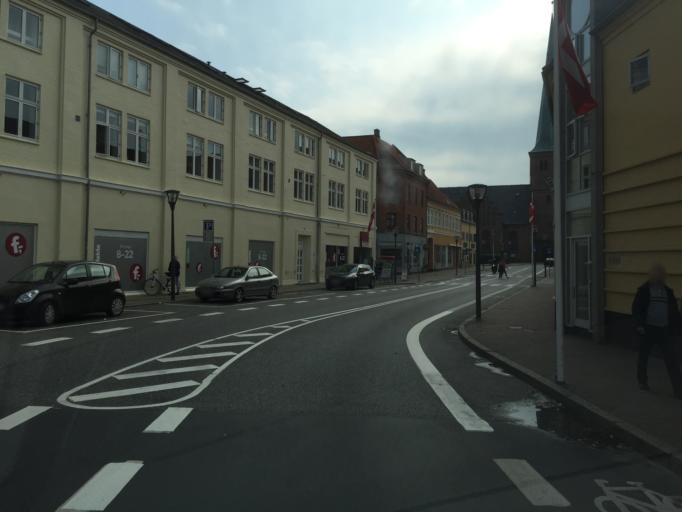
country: DK
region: South Denmark
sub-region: Nyborg Kommune
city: Nyborg
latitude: 55.3127
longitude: 10.7930
